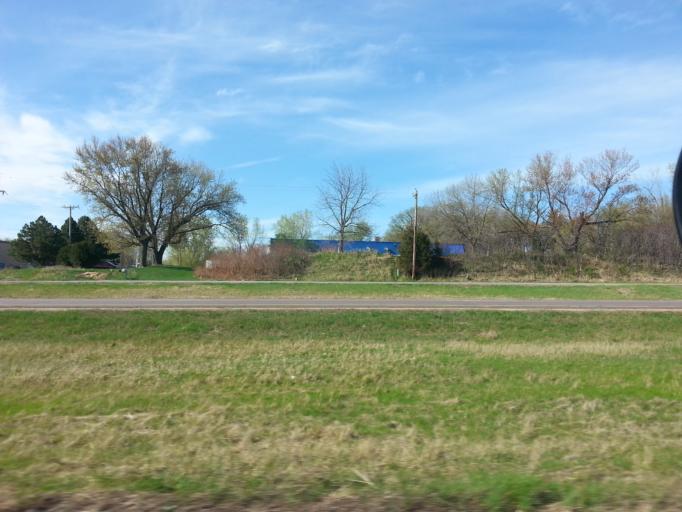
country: US
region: Minnesota
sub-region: Washington County
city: Lake Elmo
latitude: 45.0356
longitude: -92.8787
